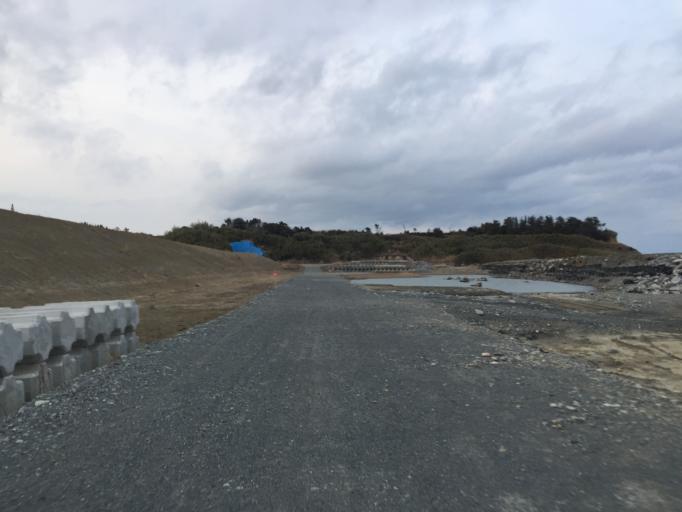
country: JP
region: Fukushima
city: Namie
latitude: 37.7600
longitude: 140.9996
